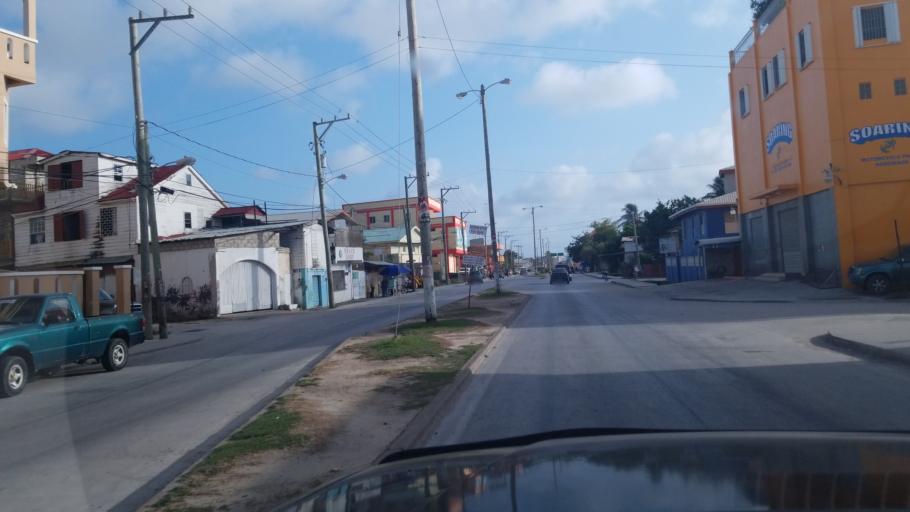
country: BZ
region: Belize
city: Belize City
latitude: 17.4926
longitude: -88.1990
